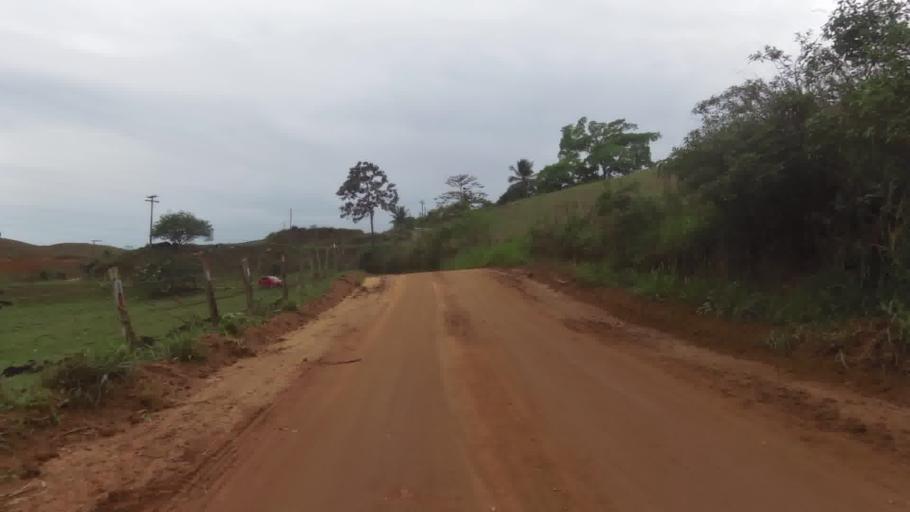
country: BR
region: Espirito Santo
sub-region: Iconha
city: Iconha
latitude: -20.7986
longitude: -40.8186
